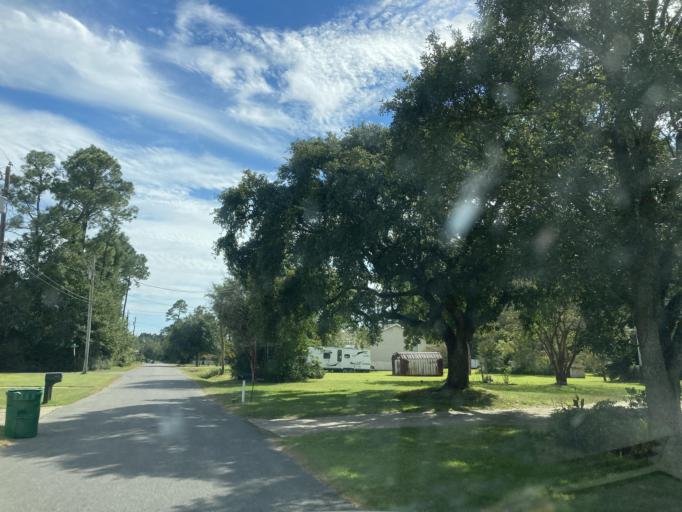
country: US
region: Mississippi
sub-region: Jackson County
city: Saint Martin
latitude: 30.4410
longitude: -88.8711
